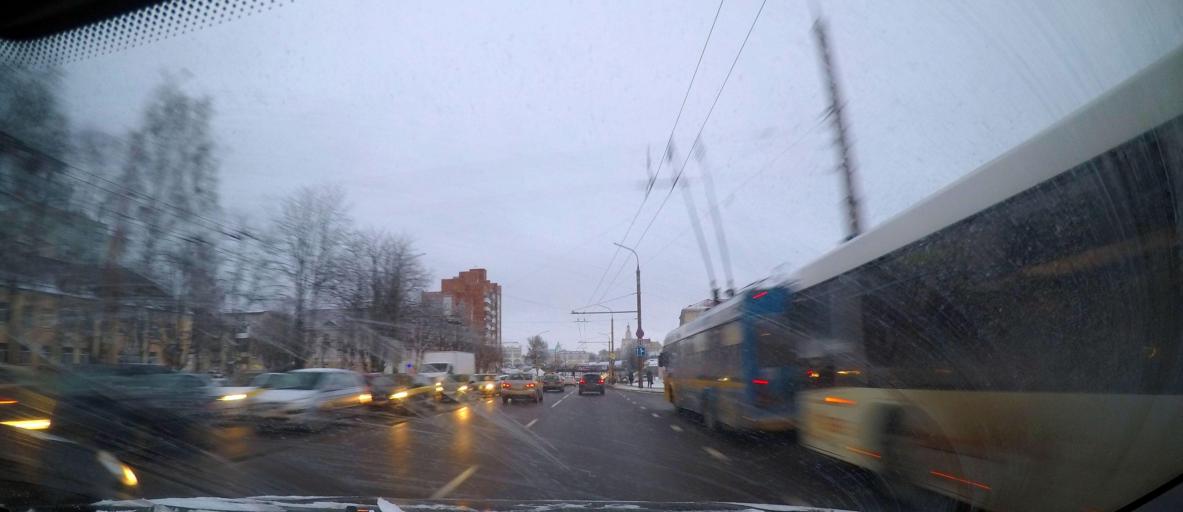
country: BY
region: Grodnenskaya
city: Hrodna
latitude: 53.6695
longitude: 23.8233
